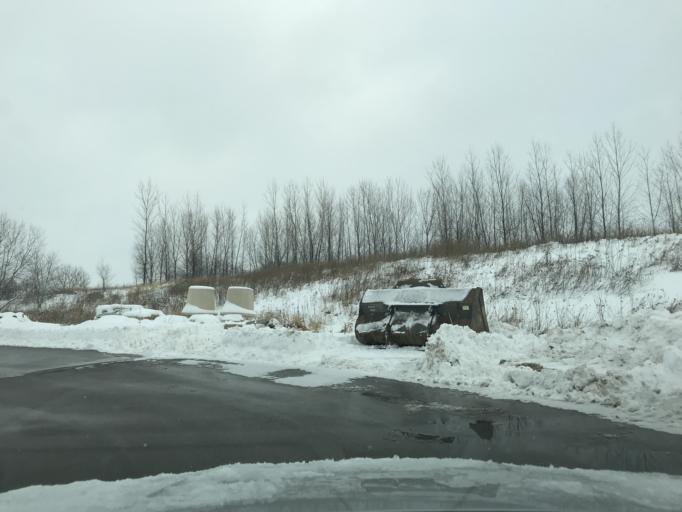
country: US
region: Wisconsin
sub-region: Dane County
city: Sun Prairie
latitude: 43.1601
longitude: -89.2816
